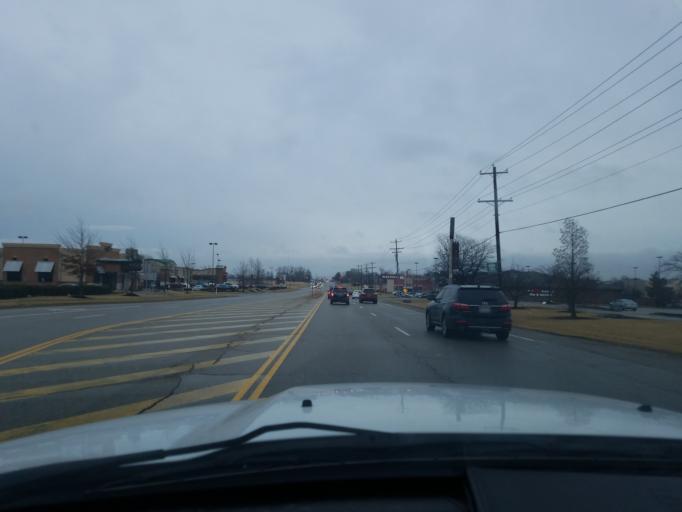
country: US
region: Ohio
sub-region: Butler County
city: Wetherington
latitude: 39.3527
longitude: -84.3635
